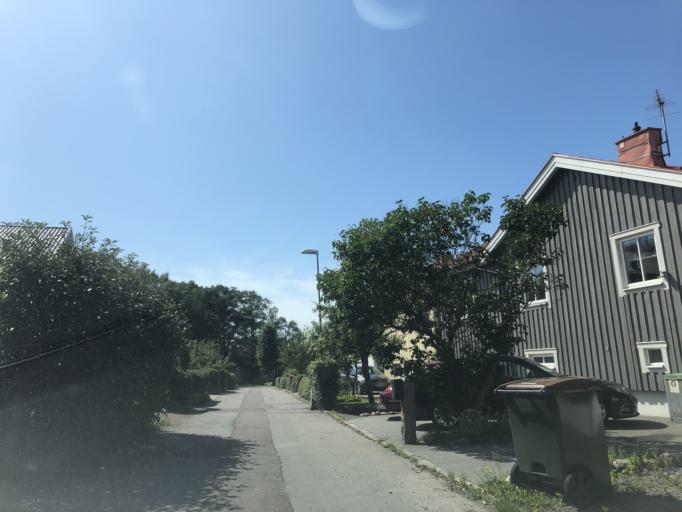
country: SE
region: Vaestra Goetaland
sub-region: Goteborg
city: Majorna
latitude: 57.7039
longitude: 11.9059
